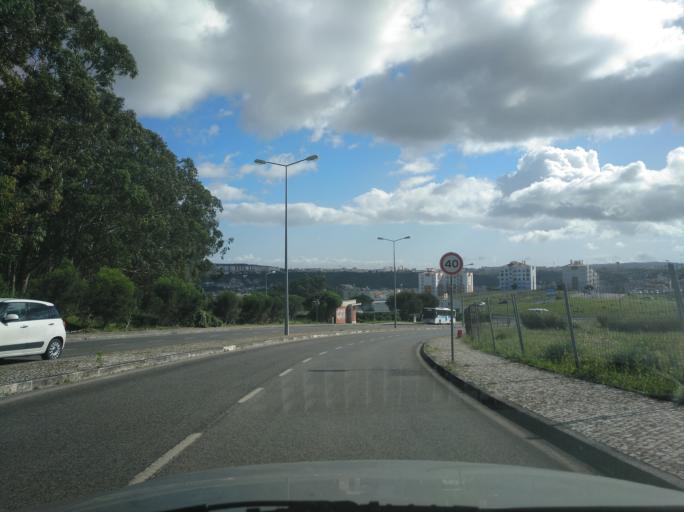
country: PT
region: Lisbon
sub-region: Odivelas
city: Povoa de Santo Adriao
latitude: 38.8090
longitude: -9.1674
